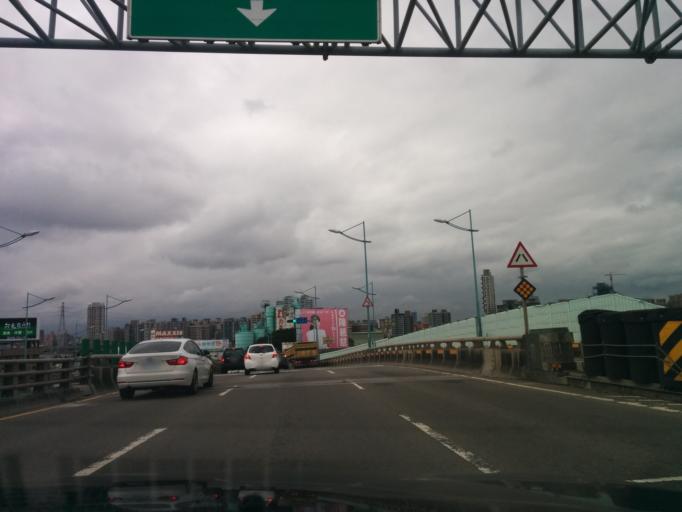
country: TW
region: Taipei
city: Taipei
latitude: 25.0968
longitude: 121.4974
